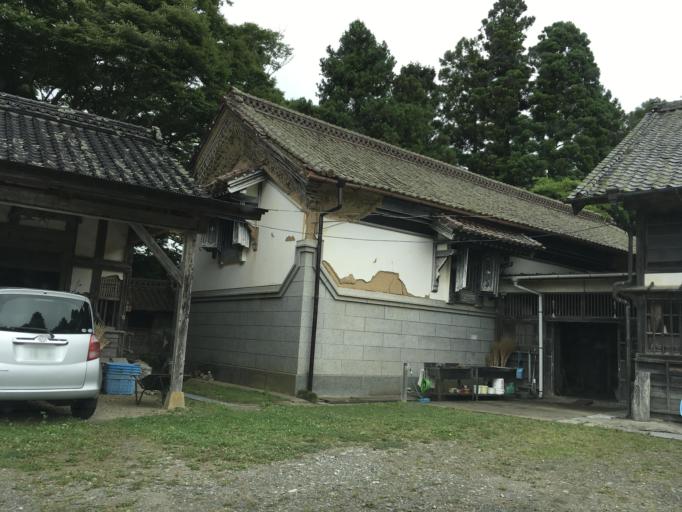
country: JP
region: Iwate
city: Ofunato
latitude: 38.8913
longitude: 141.6368
